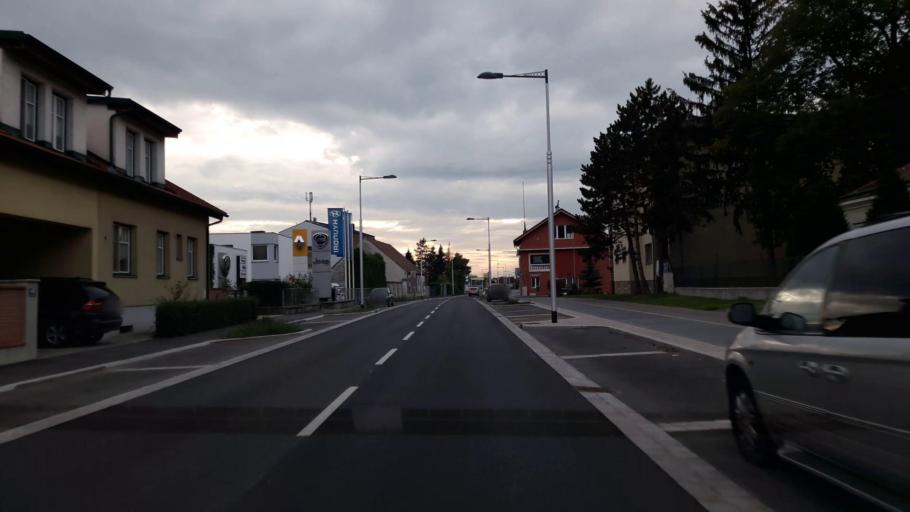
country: AT
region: Lower Austria
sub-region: Politischer Bezirk Bruck an der Leitha
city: Bruck an der Leitha
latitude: 48.0224
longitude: 16.7702
